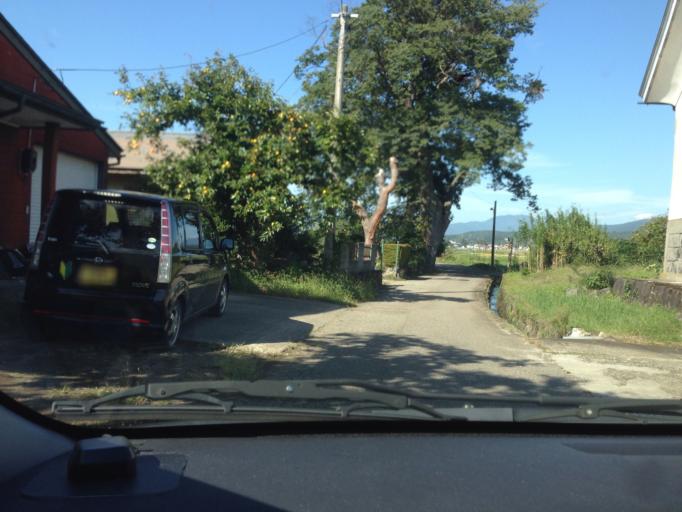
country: JP
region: Fukushima
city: Kitakata
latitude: 37.5502
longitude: 139.9158
